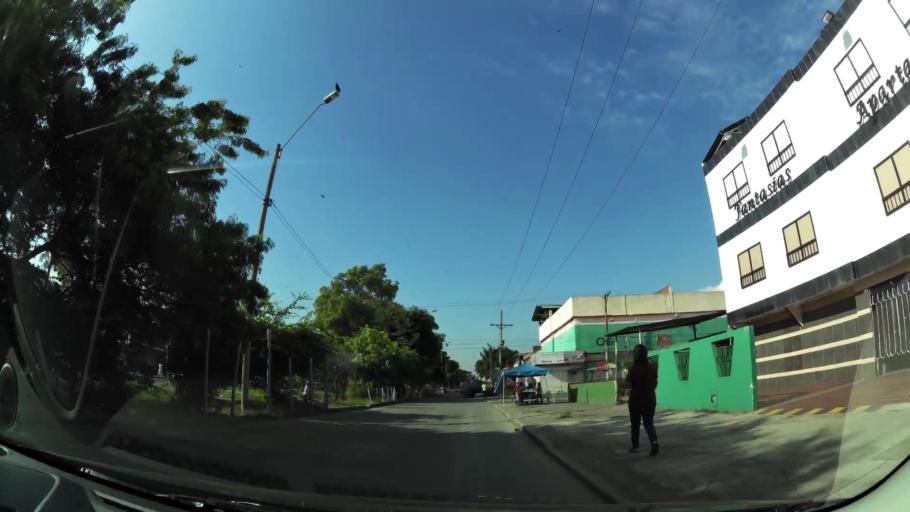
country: CO
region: Valle del Cauca
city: Cali
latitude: 3.4246
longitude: -76.5063
